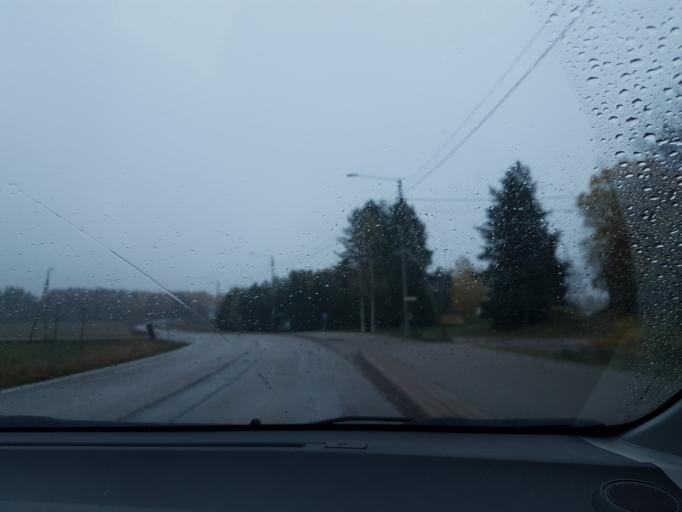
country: FI
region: Uusimaa
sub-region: Helsinki
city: Jaervenpaeae
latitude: 60.5747
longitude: 25.1533
